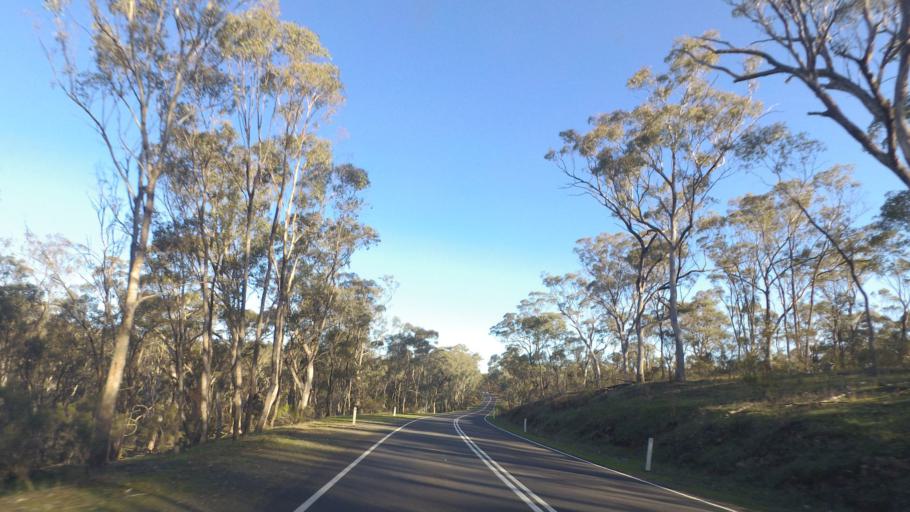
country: AU
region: Victoria
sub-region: Greater Bendigo
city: Kennington
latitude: -36.9153
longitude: 144.4924
